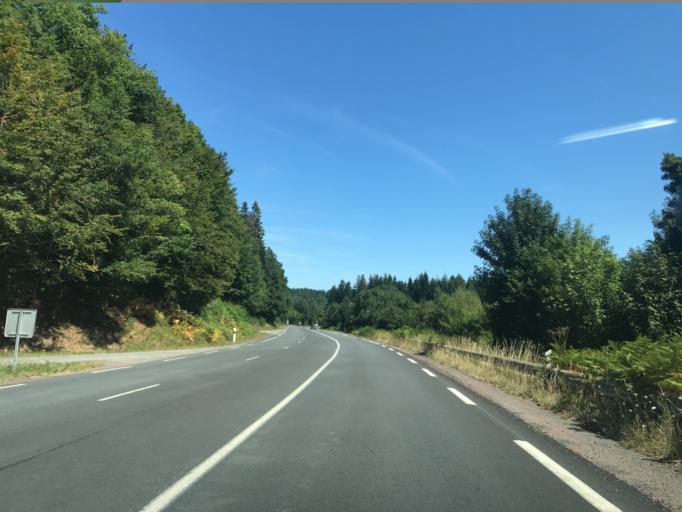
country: FR
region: Limousin
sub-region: Departement de la Correze
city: Egletons
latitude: 45.4413
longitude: 2.0997
